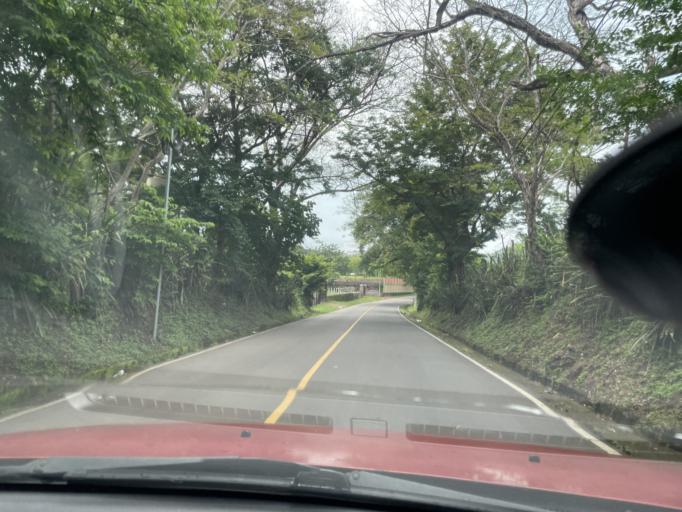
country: SV
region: La Union
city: Santa Rosa de Lima
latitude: 13.6463
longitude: -87.8553
